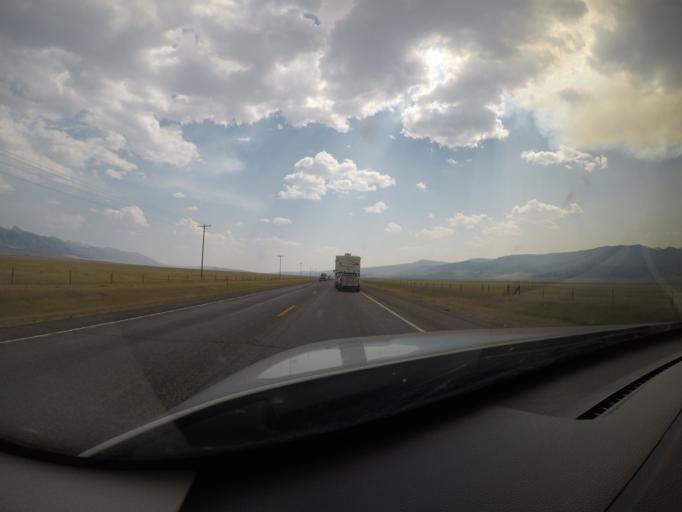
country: US
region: Montana
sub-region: Gallatin County
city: Big Sky
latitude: 45.0326
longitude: -111.6482
